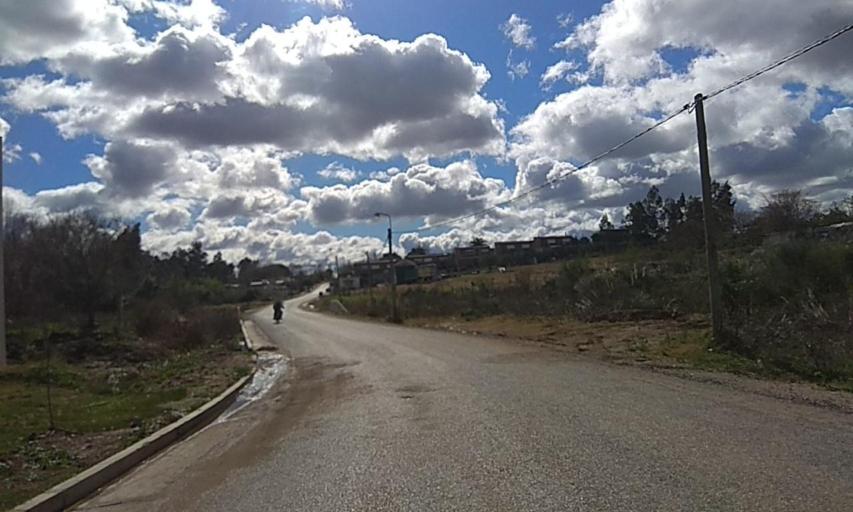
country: UY
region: Florida
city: Florida
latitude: -34.0893
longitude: -56.2262
